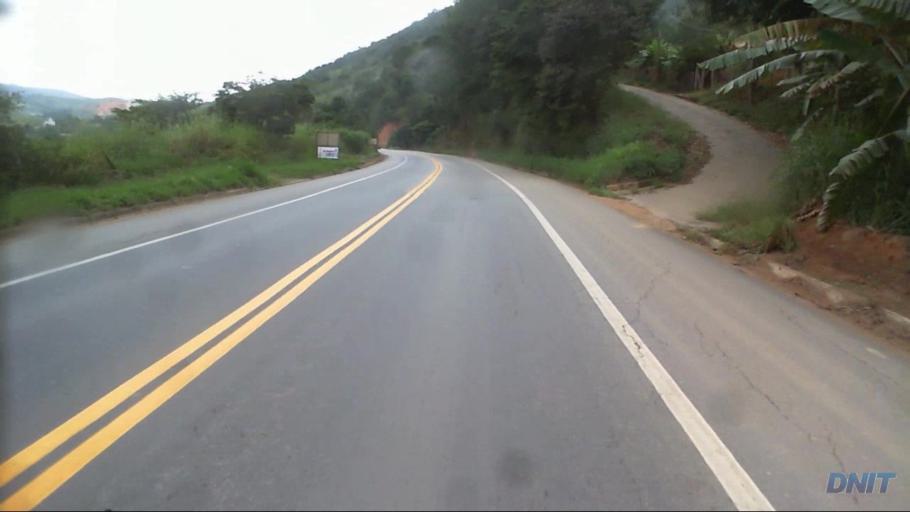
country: BR
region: Minas Gerais
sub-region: Nova Era
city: Nova Era
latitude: -19.7298
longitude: -43.0153
